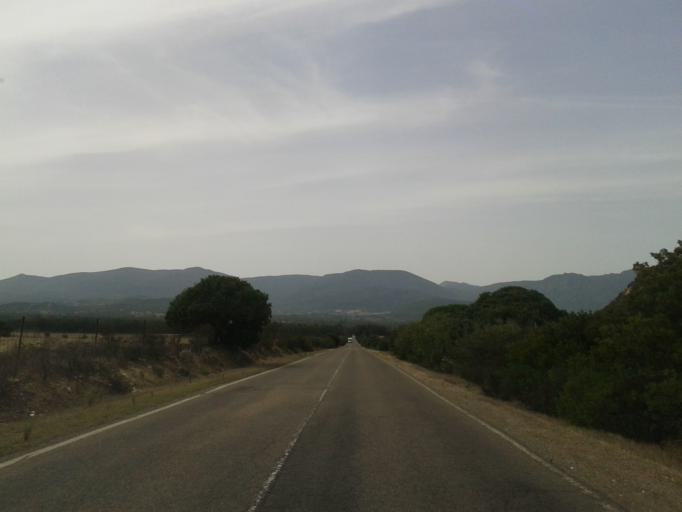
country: IT
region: Sardinia
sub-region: Provincia di Cagliari
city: Olia Speciosa
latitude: 39.2826
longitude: 9.5572
